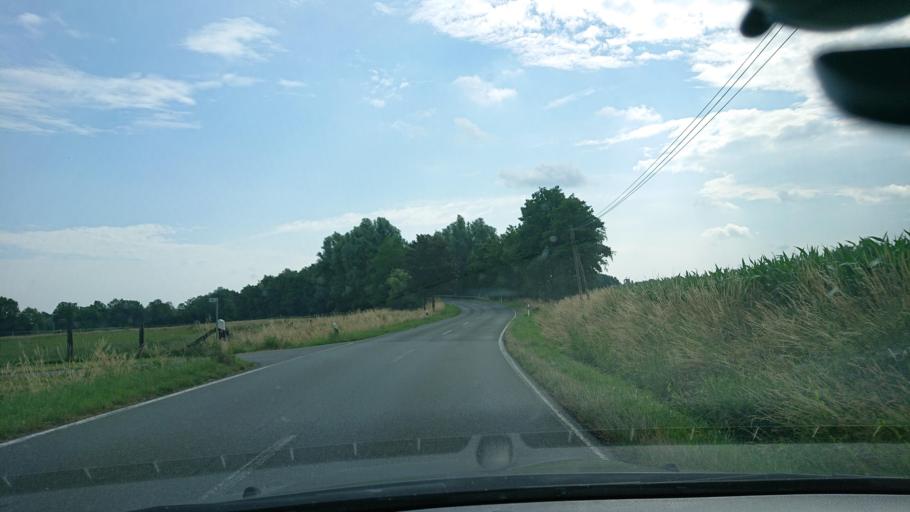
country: DE
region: North Rhine-Westphalia
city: Rietberg
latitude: 51.7950
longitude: 8.4116
